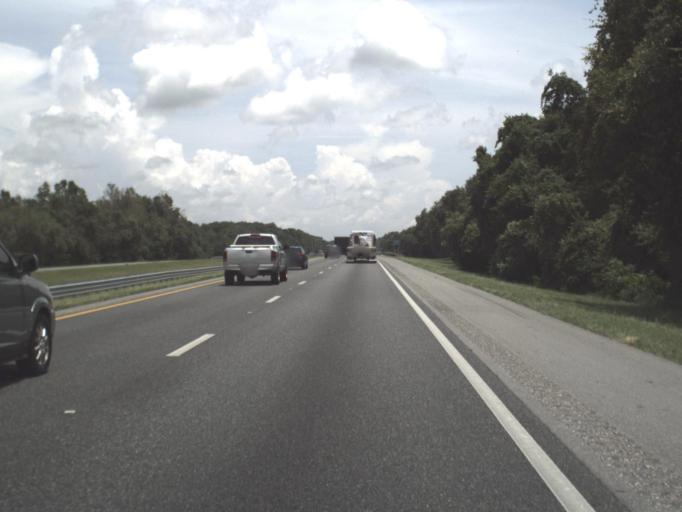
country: US
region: Florida
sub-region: Hernando County
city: Ridge Manor
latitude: 28.5775
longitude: -82.2194
